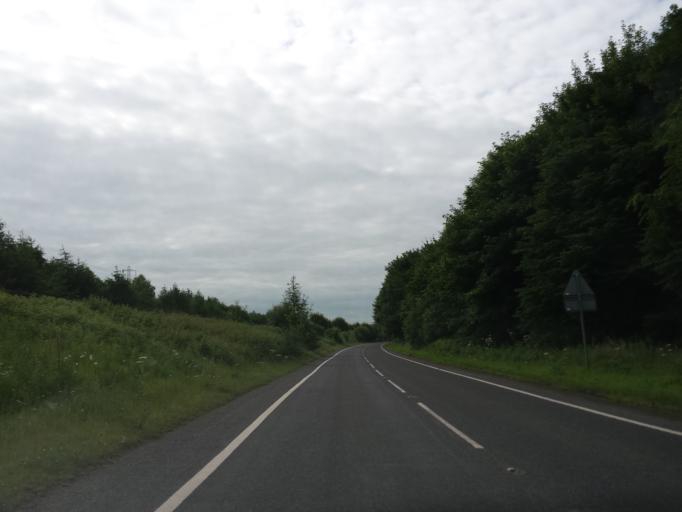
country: GB
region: Scotland
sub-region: Dumfries and Galloway
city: Moffat
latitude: 55.3238
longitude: -3.4695
